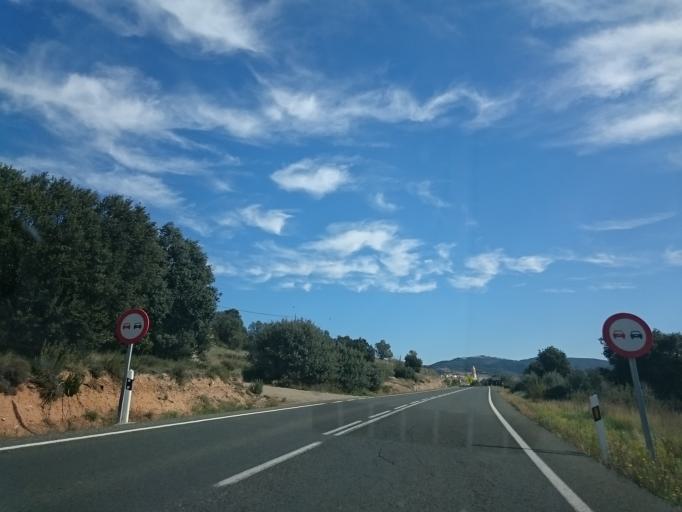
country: ES
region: Aragon
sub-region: Provincia de Huesca
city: Benavarri / Benabarre
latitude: 42.1132
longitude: 0.5550
